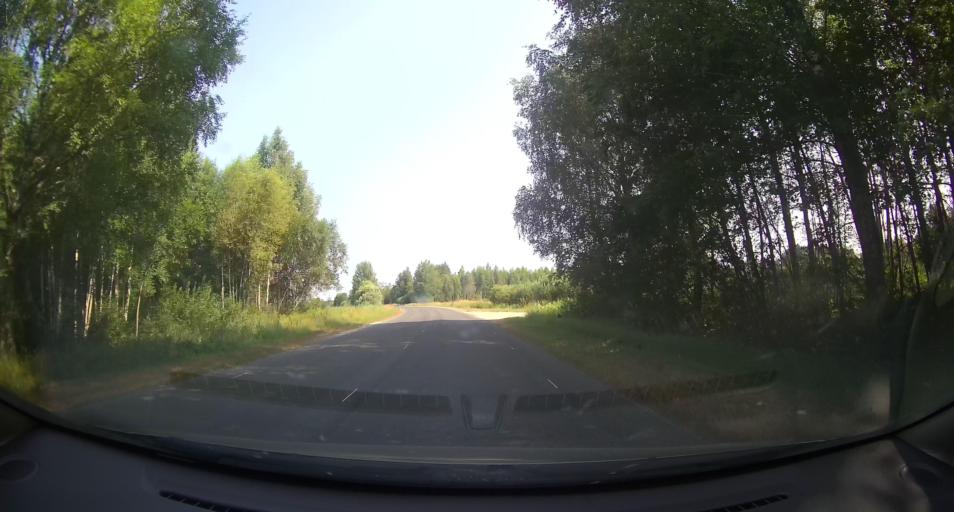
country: EE
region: Paernumaa
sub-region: Audru vald
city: Audru
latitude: 58.4526
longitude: 24.3156
